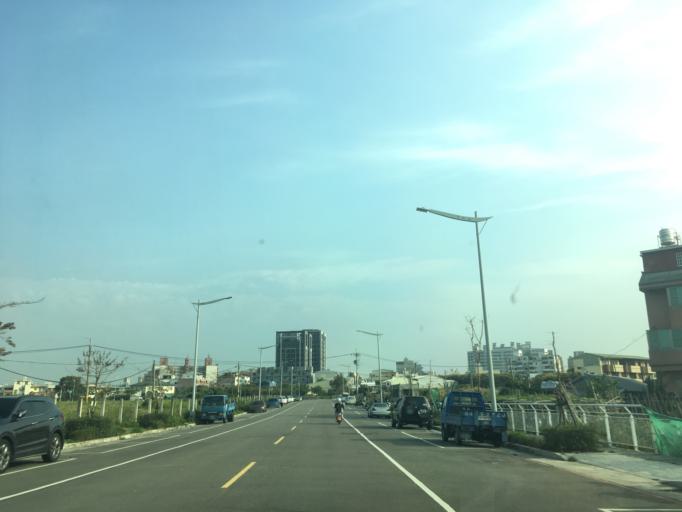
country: TW
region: Taiwan
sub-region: Taichung City
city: Taichung
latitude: 24.1885
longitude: 120.6976
